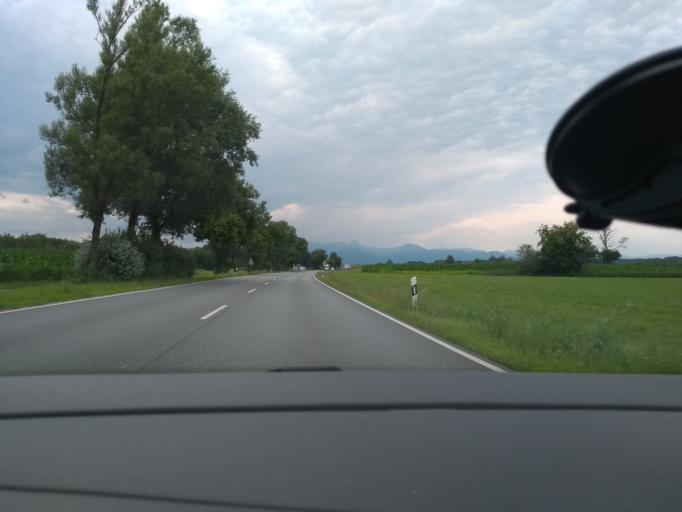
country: DE
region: Bavaria
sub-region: Upper Bavaria
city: Schechen
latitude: 47.9076
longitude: 12.1270
